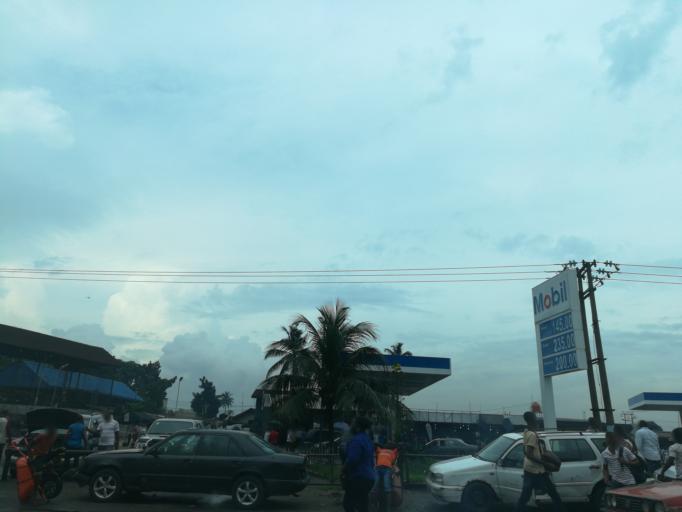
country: NG
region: Rivers
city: Port Harcourt
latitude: 4.8166
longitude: 7.0095
